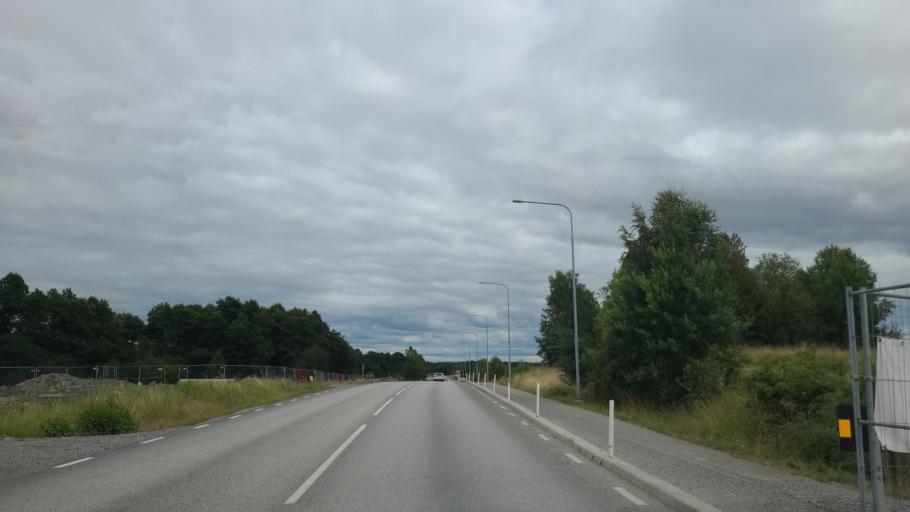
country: SE
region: Stockholm
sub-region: Upplands-Bro Kommun
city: Bro
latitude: 59.5119
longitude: 17.6238
